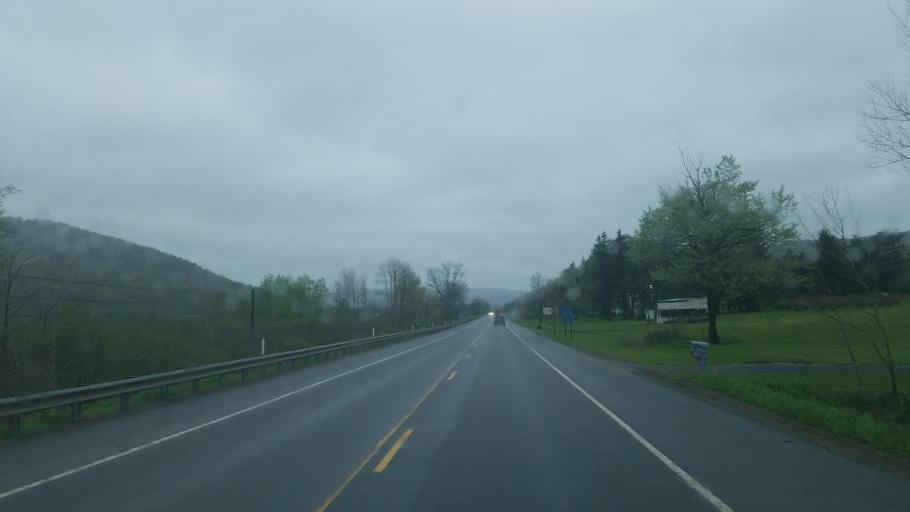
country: US
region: Pennsylvania
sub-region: McKean County
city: Port Allegany
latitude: 41.7906
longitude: -78.2404
